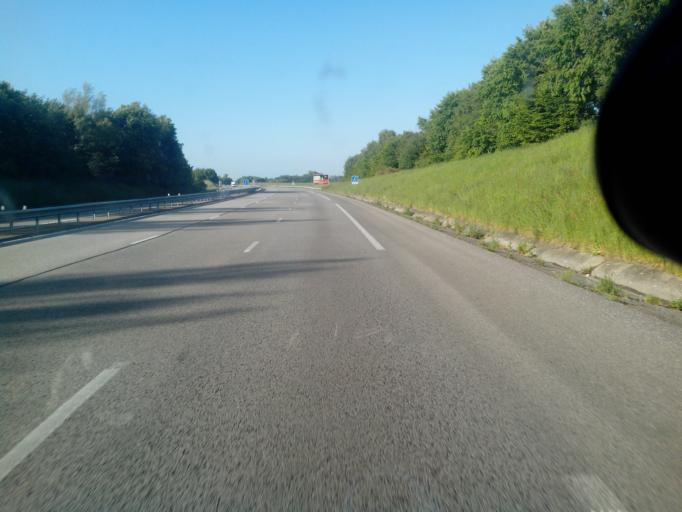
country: FR
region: Haute-Normandie
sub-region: Departement de la Seine-Maritime
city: Saint-Aubin-Routot
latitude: 49.5251
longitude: 0.3081
